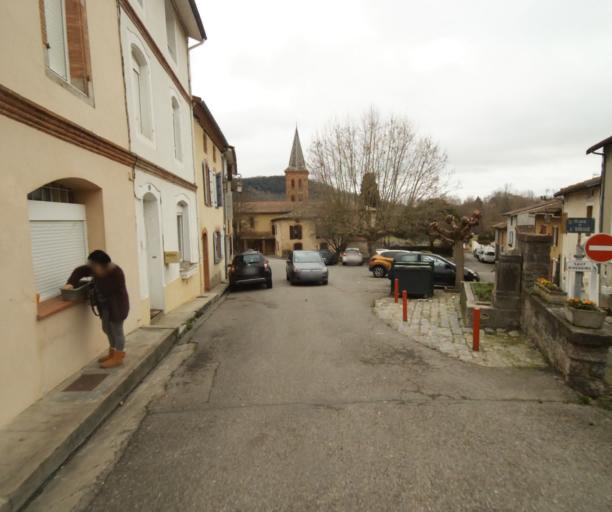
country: FR
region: Midi-Pyrenees
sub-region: Departement de l'Ariege
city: Pamiers
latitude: 43.1659
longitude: 1.5916
